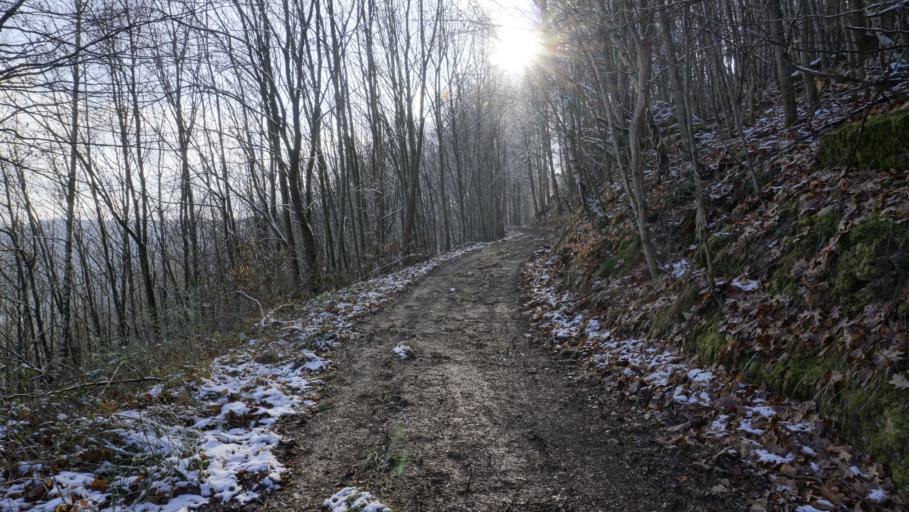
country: DE
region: Baden-Wuerttemberg
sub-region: Karlsruhe Region
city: Zwingenberg
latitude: 49.4131
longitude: 9.0365
